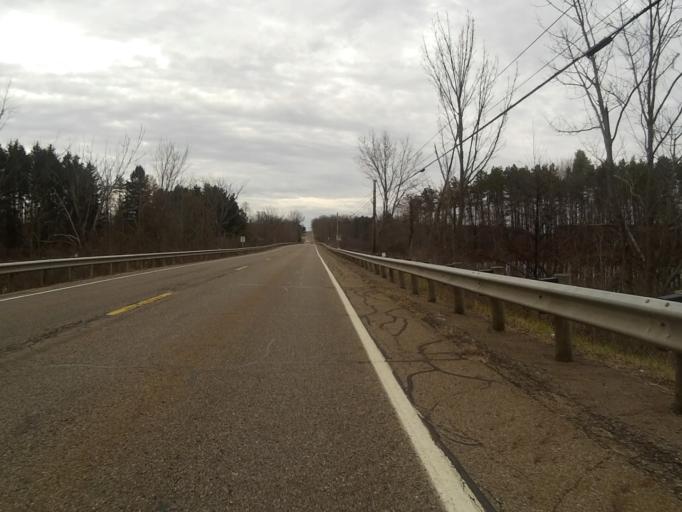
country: US
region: Ohio
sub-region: Portage County
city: Brimfield
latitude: 41.0536
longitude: -81.3474
